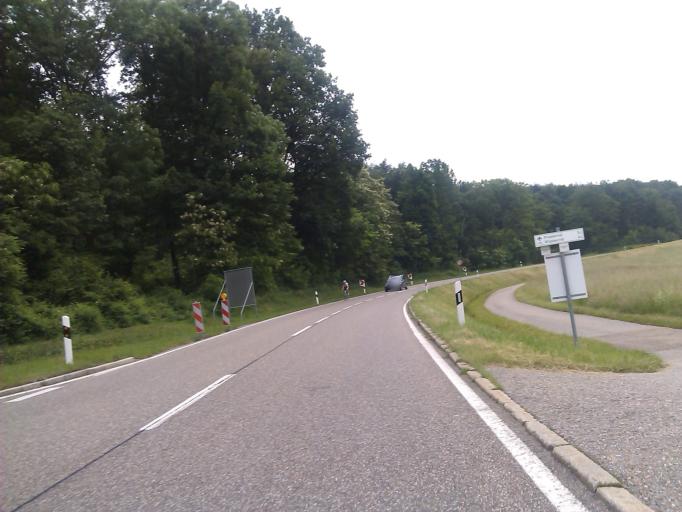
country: DE
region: Baden-Wuerttemberg
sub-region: Regierungsbezirk Stuttgart
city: Lowenstein
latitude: 49.1008
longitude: 9.4297
